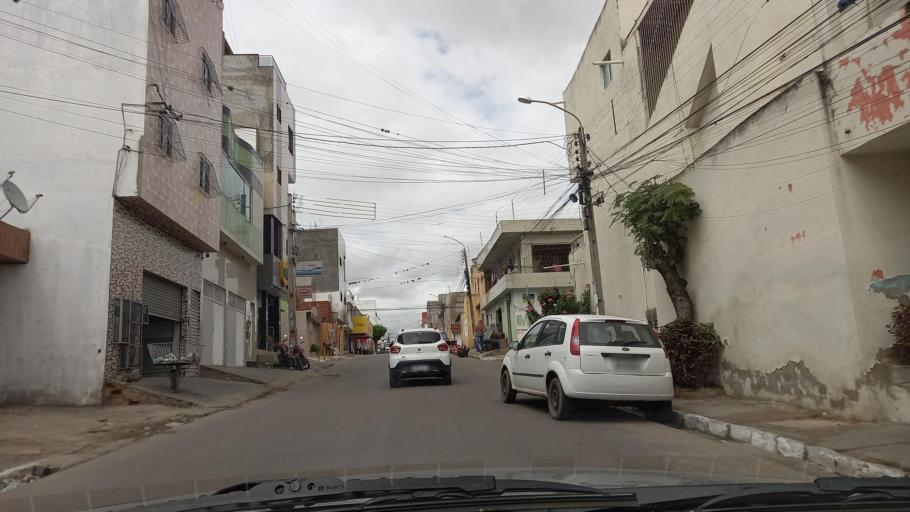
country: BR
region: Pernambuco
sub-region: Caruaru
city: Caruaru
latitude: -8.2760
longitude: -35.9601
